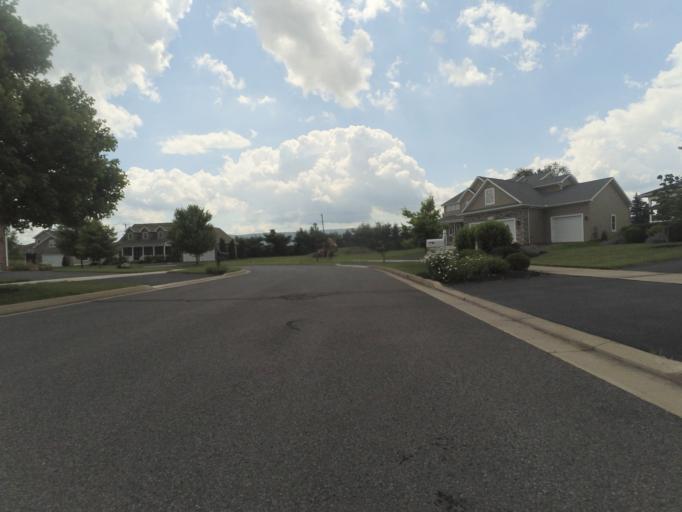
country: US
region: Pennsylvania
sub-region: Centre County
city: State College
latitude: 40.7785
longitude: -77.8439
